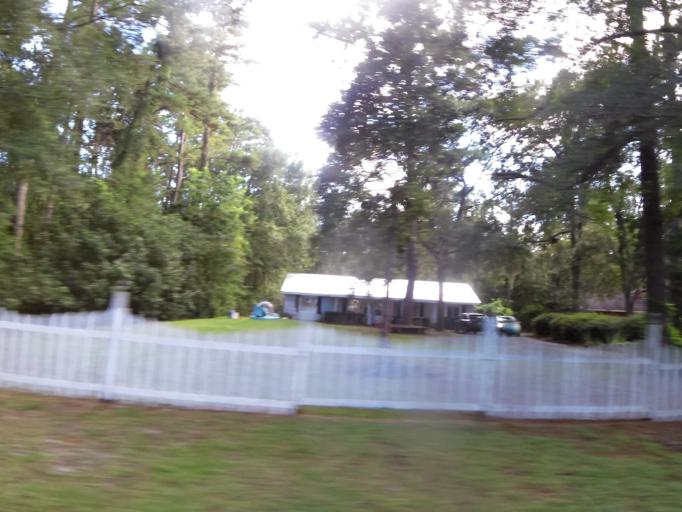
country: US
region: Georgia
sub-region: Glynn County
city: Country Club Estates
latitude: 31.2568
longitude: -81.4376
